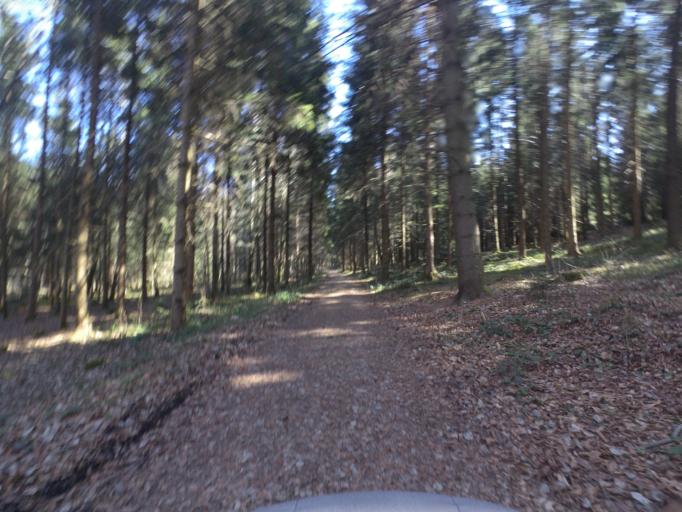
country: AT
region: Salzburg
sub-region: Politischer Bezirk Salzburg-Umgebung
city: Mattsee
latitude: 47.9920
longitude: 13.1071
